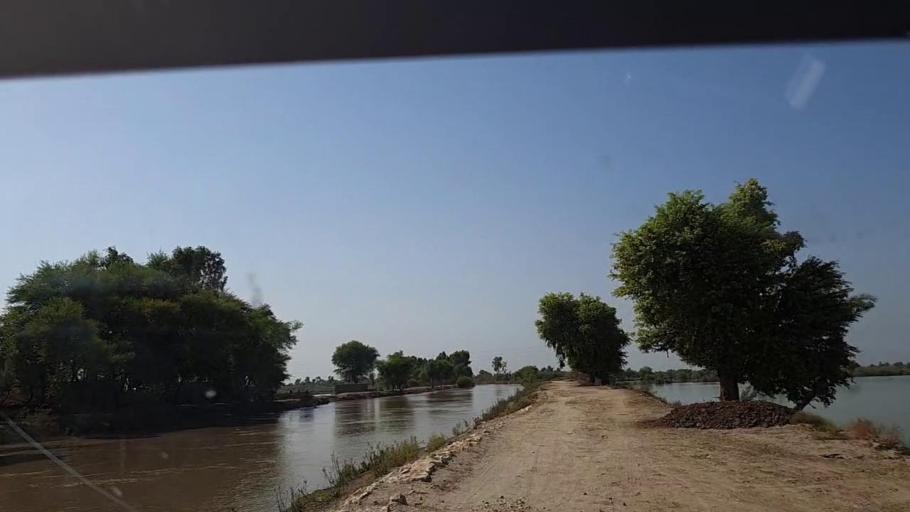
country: PK
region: Sindh
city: Ghauspur
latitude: 28.1813
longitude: 69.0857
